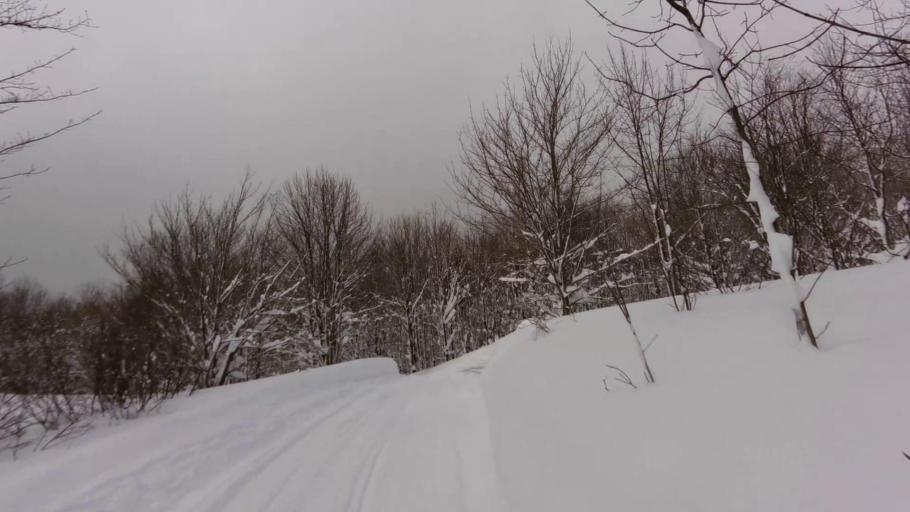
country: US
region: New York
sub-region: Lewis County
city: Lowville
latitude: 43.7559
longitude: -75.6794
